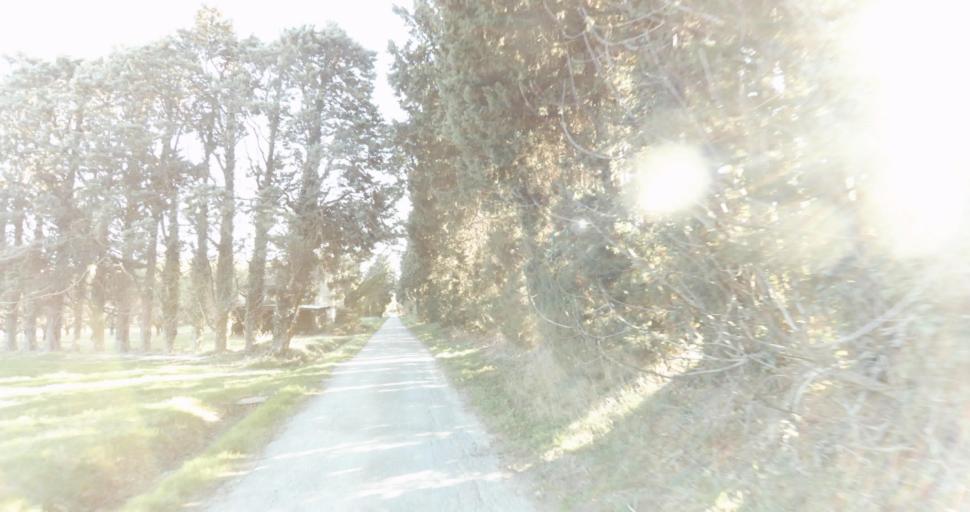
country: FR
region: Provence-Alpes-Cote d'Azur
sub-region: Departement des Bouches-du-Rhone
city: Barbentane
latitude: 43.9184
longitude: 4.7455
